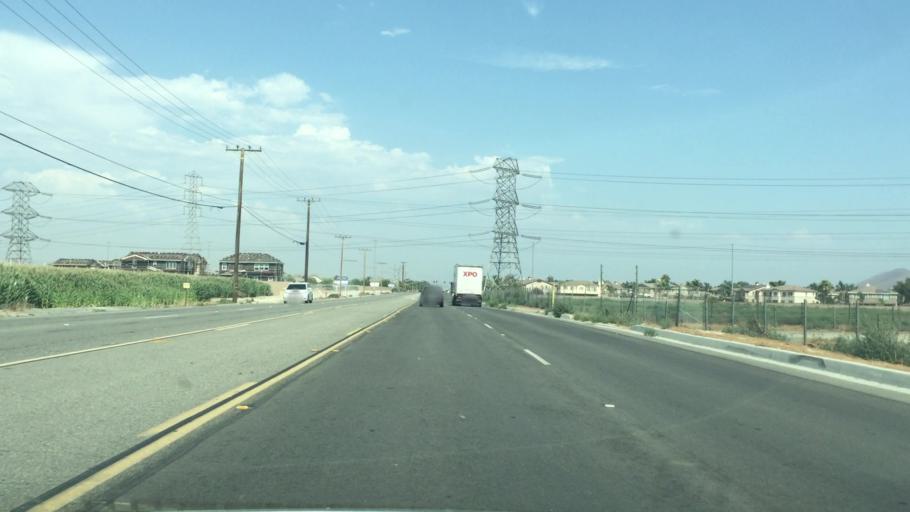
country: US
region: California
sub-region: Riverside County
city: Norco
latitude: 33.9753
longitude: -117.5910
